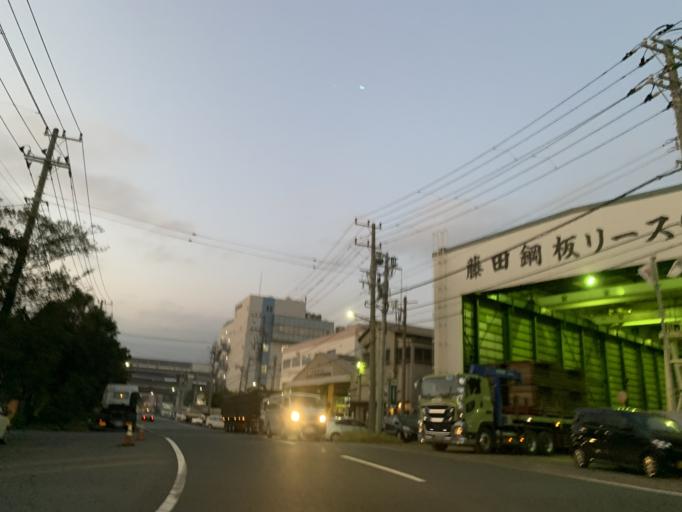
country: JP
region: Chiba
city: Funabashi
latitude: 35.6855
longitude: 139.9504
